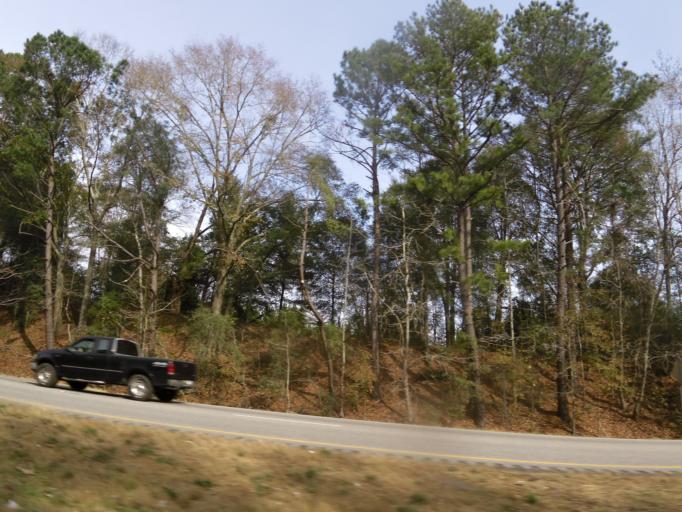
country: US
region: Alabama
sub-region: Dale County
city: Newton
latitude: 31.3938
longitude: -85.5857
